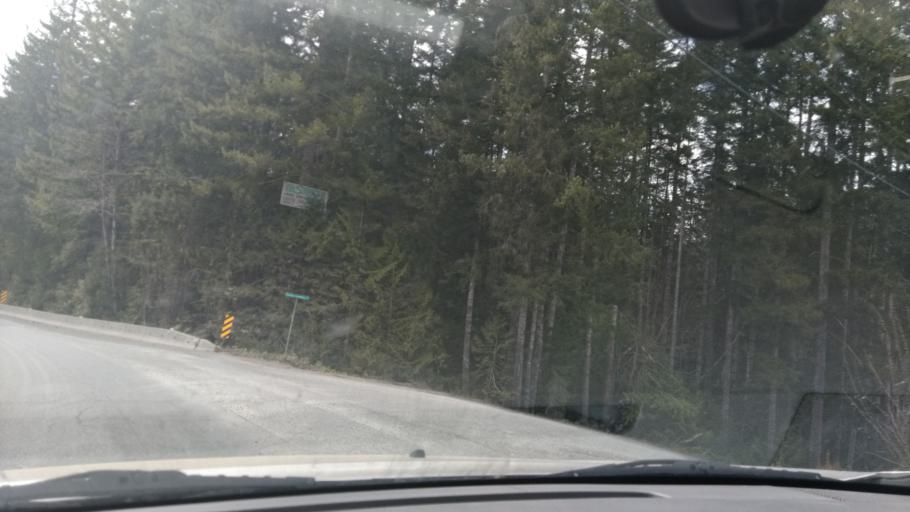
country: CA
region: British Columbia
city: Campbell River
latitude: 49.9976
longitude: -125.3788
